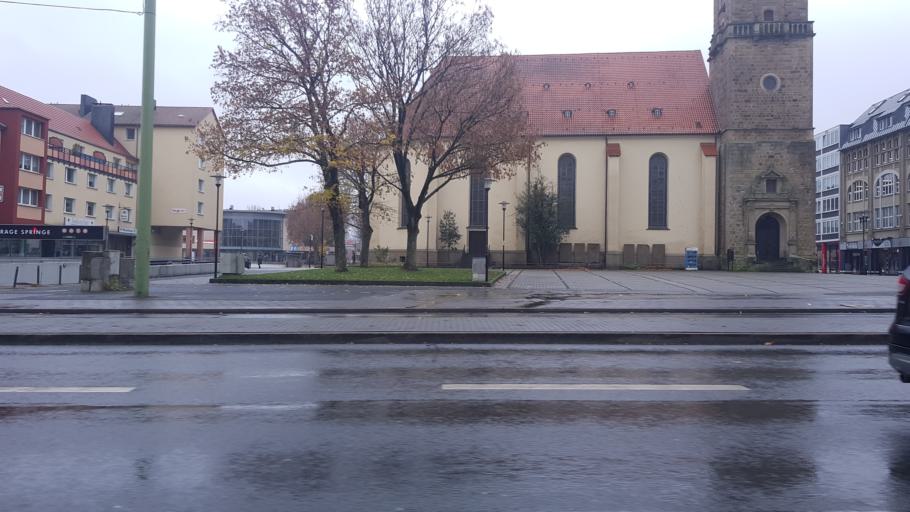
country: DE
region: North Rhine-Westphalia
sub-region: Regierungsbezirk Arnsberg
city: Hagen
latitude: 51.3563
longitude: 7.4771
